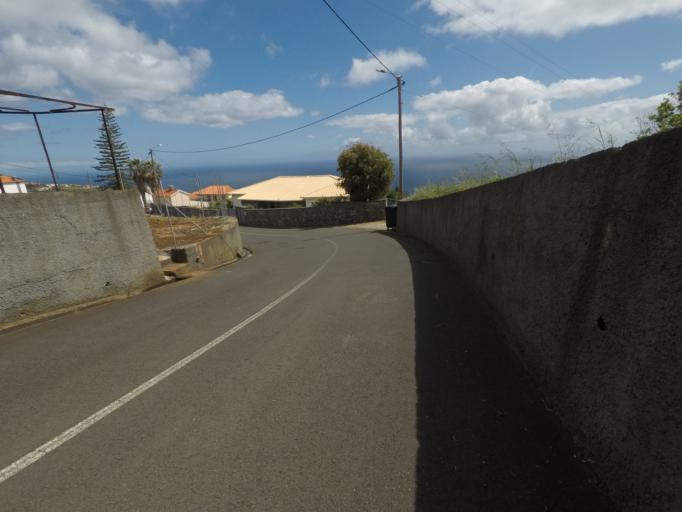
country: PT
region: Madeira
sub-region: Calheta
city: Estreito da Calheta
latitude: 32.7328
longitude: -17.1840
